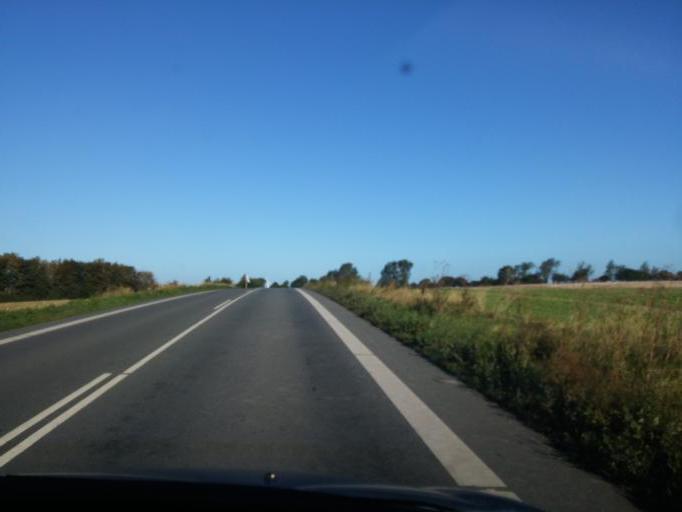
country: DK
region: South Denmark
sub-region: Kerteminde Kommune
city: Kerteminde
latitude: 55.4724
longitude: 10.6701
